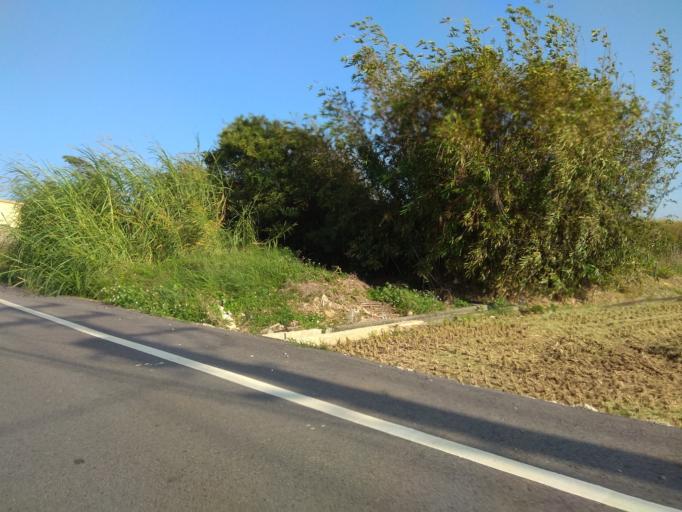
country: TW
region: Taiwan
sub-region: Hsinchu
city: Zhubei
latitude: 24.9916
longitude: 121.0700
